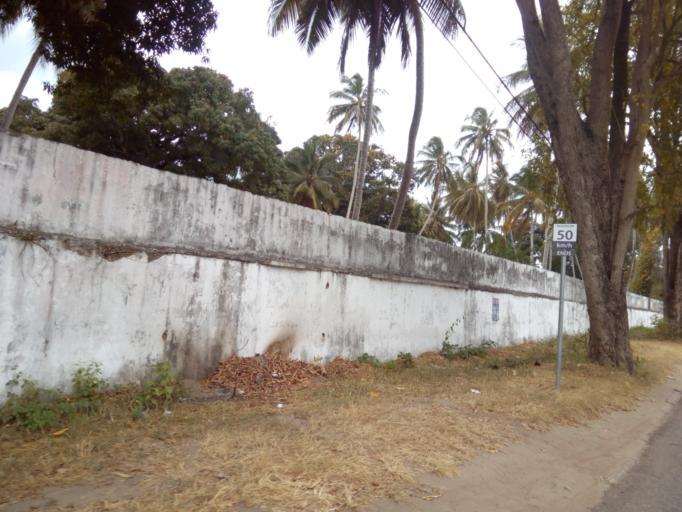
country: TZ
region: Zanzibar Urban/West
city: Zanzibar
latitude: -6.1859
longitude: 39.2063
